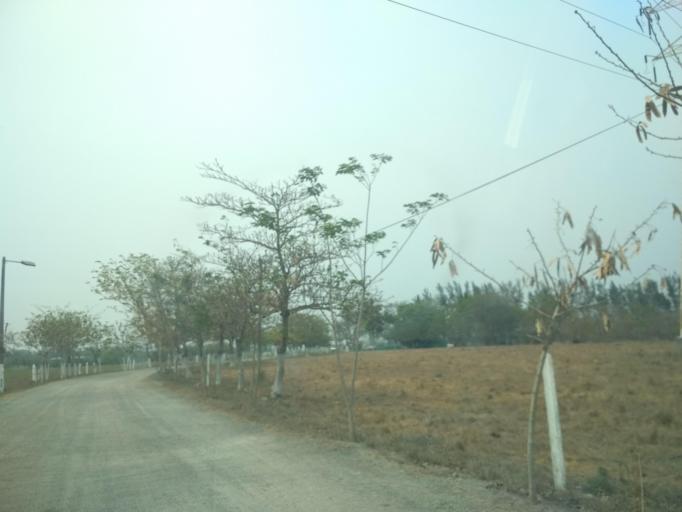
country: MX
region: Veracruz
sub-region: Veracruz
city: Las Amapolas
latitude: 19.1658
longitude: -96.2088
